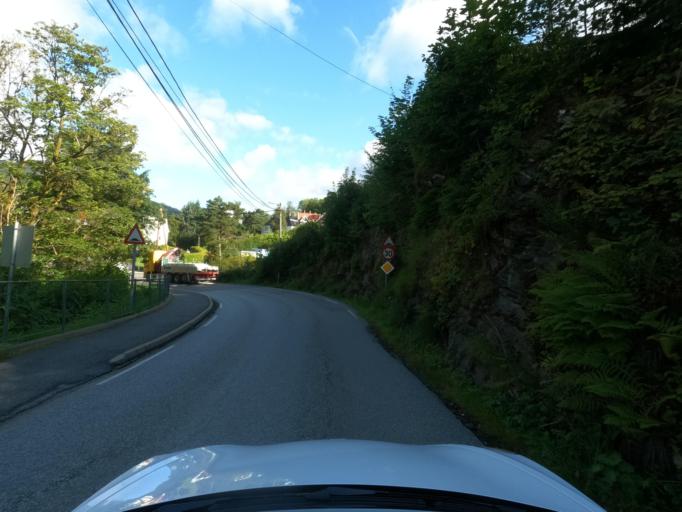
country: NO
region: Hordaland
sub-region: Bergen
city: Bergen
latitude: 60.3396
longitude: 5.3438
